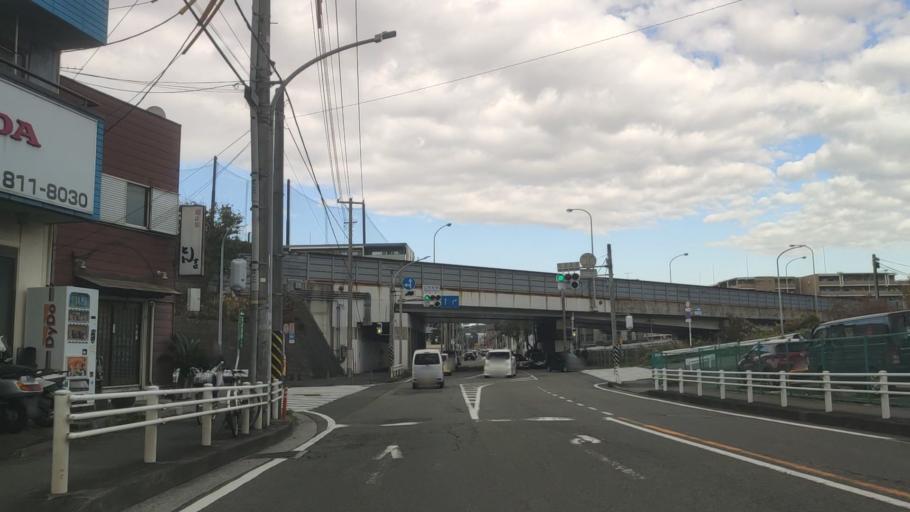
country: JP
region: Kanagawa
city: Fujisawa
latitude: 35.4177
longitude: 139.5380
